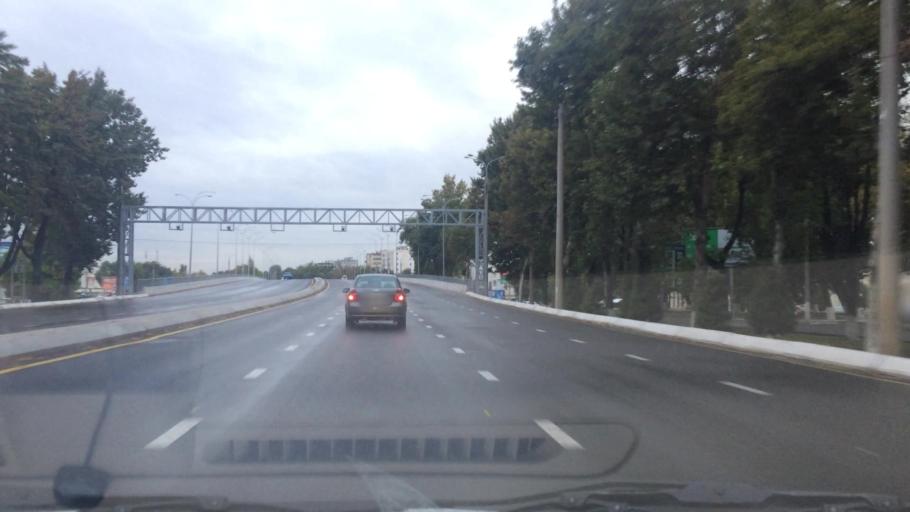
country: UZ
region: Toshkent Shahri
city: Tashkent
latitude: 41.2765
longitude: 69.2063
